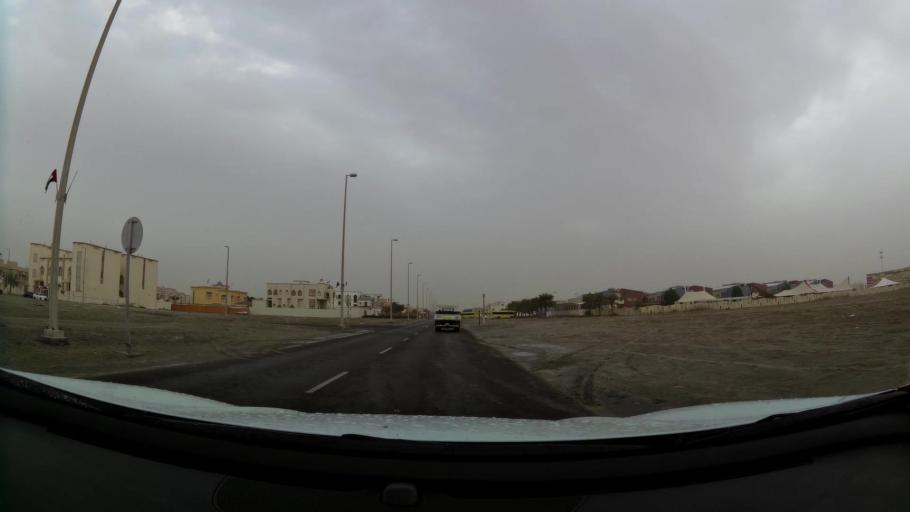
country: AE
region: Abu Dhabi
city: Abu Dhabi
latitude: 24.4092
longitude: 54.5874
